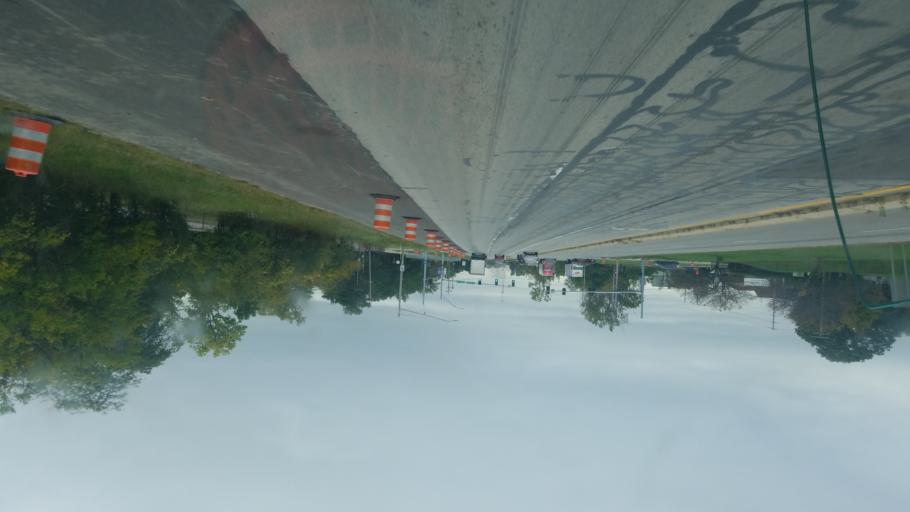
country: US
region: Ohio
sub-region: Lucas County
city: Maumee
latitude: 41.5575
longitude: -83.6760
